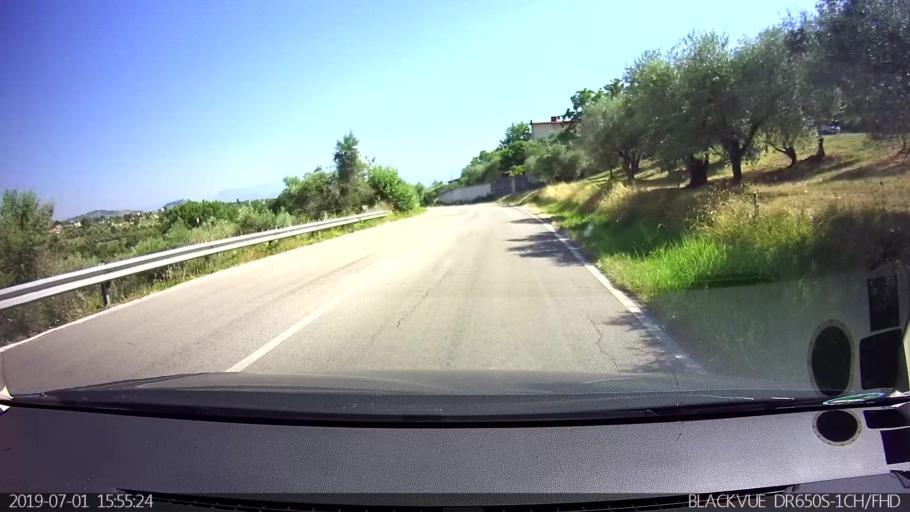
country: IT
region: Latium
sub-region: Provincia di Frosinone
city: Veroli
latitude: 41.6889
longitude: 13.4223
